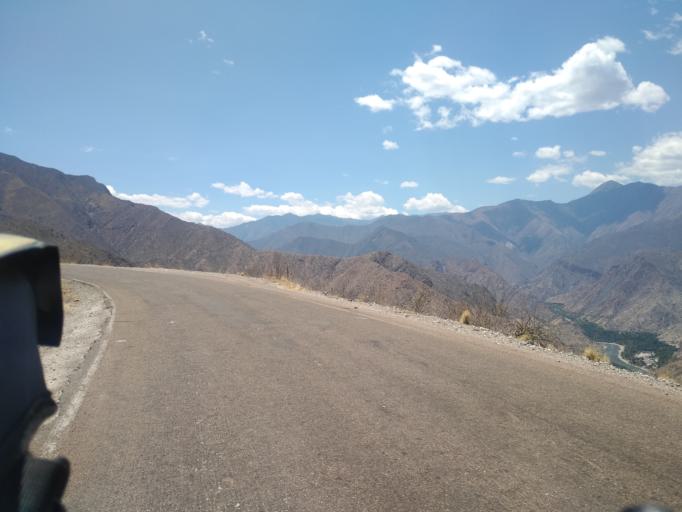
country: PE
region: Amazonas
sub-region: Provincia de Chachapoyas
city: Balsas
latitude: -6.8470
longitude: -78.0438
